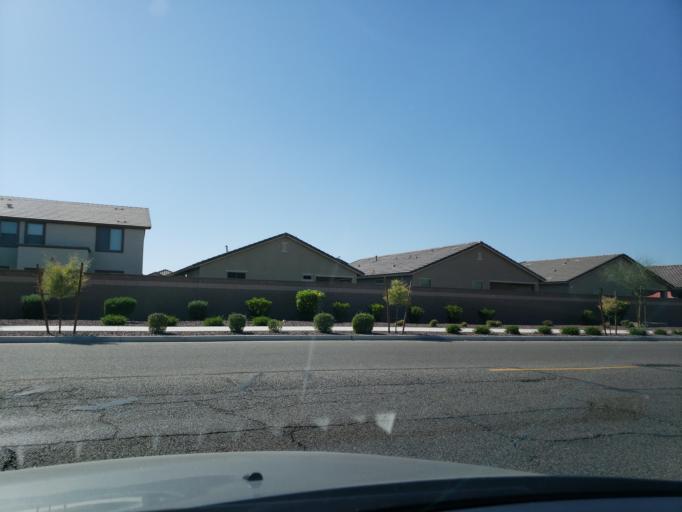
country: US
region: Arizona
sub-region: Maricopa County
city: Glendale
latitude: 33.5600
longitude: -112.1905
